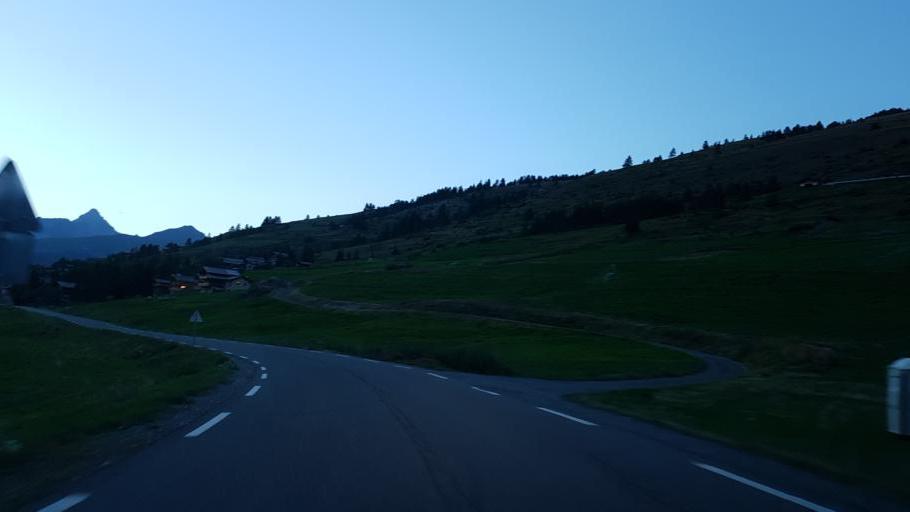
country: FR
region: Provence-Alpes-Cote d'Azur
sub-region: Departement des Hautes-Alpes
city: Guillestre
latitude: 44.7245
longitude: 6.8475
